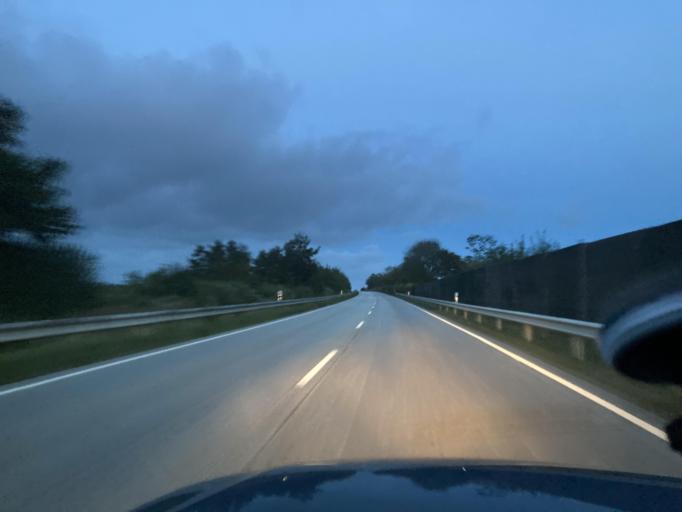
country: DE
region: Schleswig-Holstein
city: Tonning
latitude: 54.3247
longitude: 8.9290
